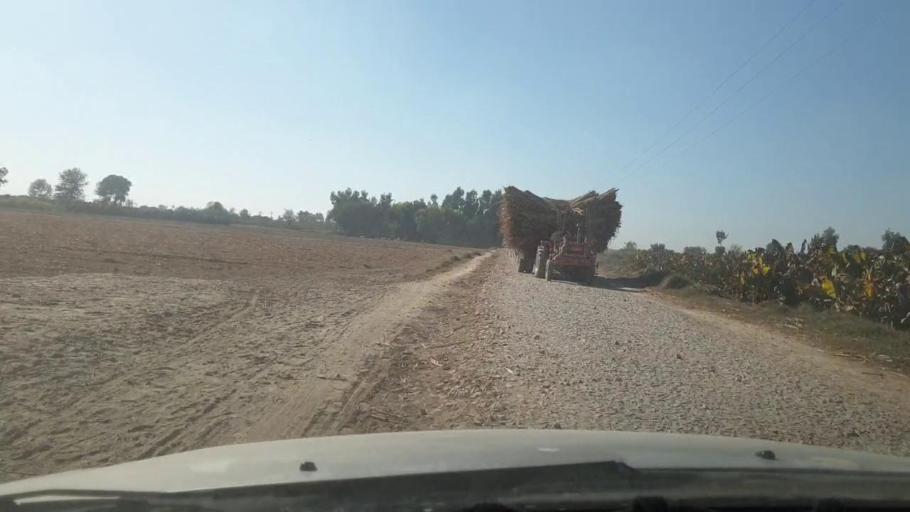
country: PK
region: Sindh
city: Ghotki
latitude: 27.9855
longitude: 69.2252
